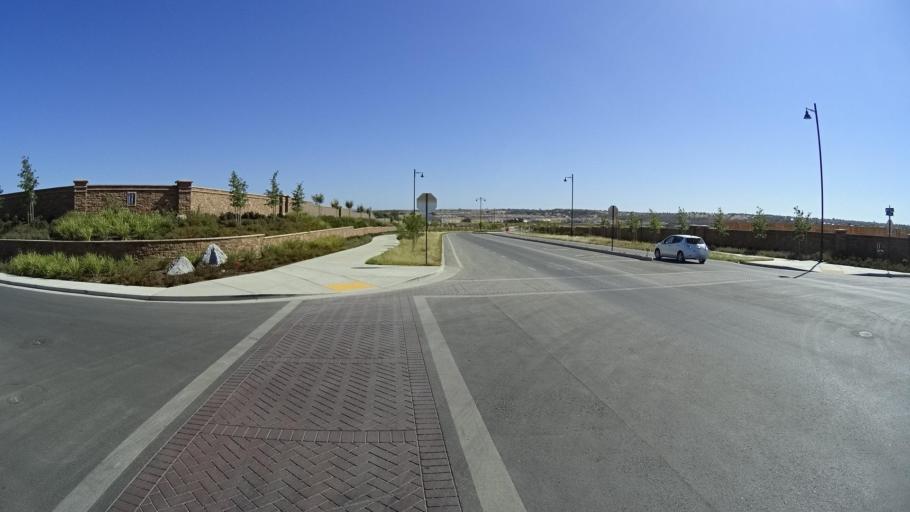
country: US
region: California
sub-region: Placer County
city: Rocklin
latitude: 38.8354
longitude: -121.2630
